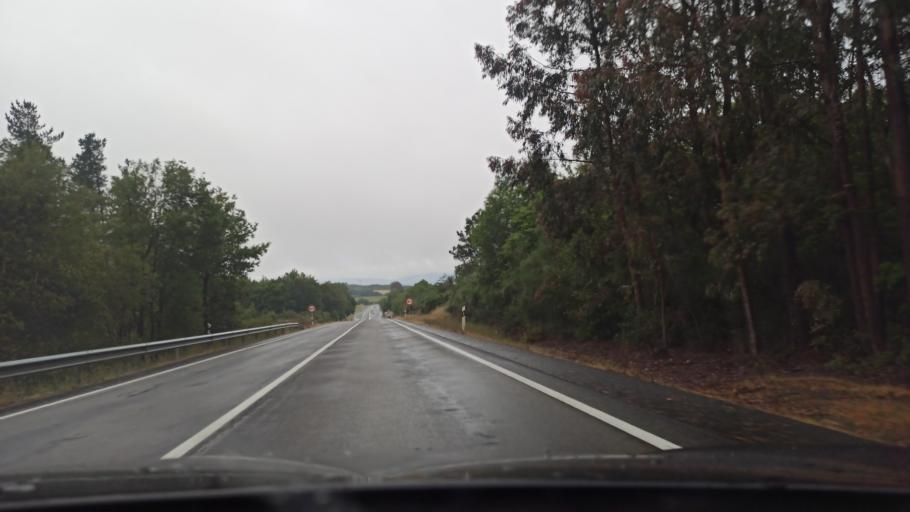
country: ES
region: Galicia
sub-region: Provincia de Lugo
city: Monterroso
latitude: 42.8138
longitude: -7.7679
